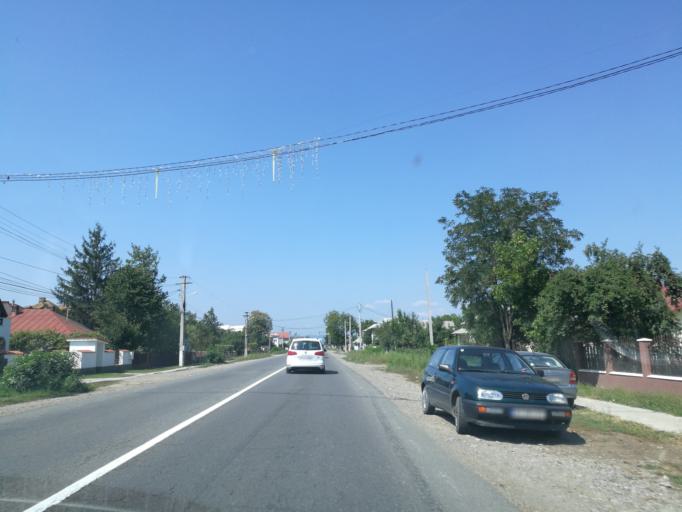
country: RO
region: Neamt
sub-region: Comuna Roznov
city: Roznov
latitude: 46.8400
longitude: 26.5040
